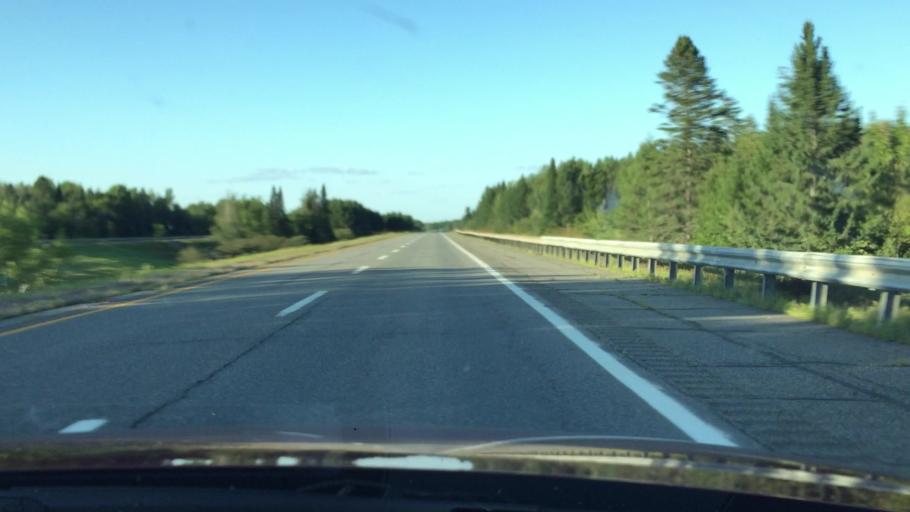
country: US
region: Maine
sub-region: Penobscot County
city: Patten
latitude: 45.8580
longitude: -68.4222
